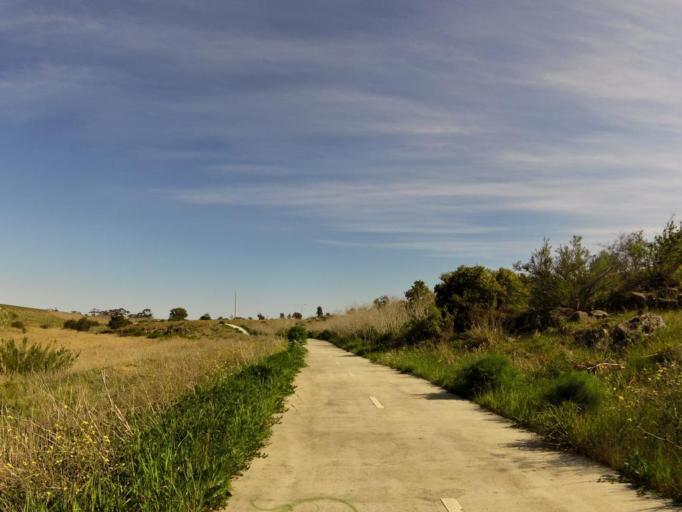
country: AU
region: Victoria
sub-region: Brimbank
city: Brooklyn
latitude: -37.8122
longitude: 144.8281
